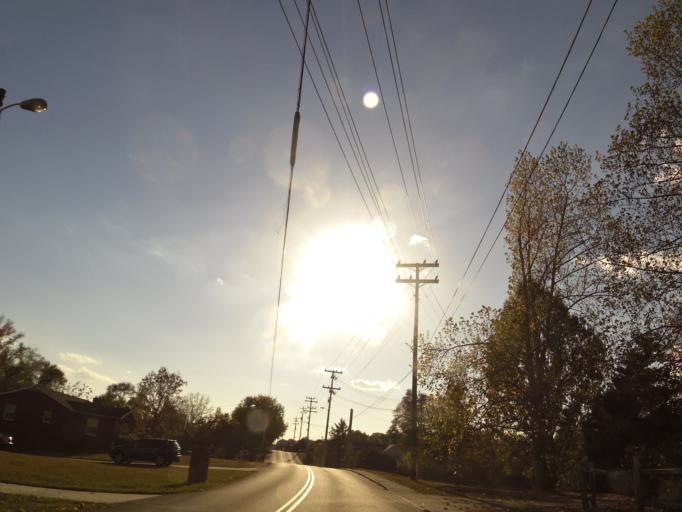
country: US
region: Tennessee
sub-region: Anderson County
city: Clinton
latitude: 36.1148
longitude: -84.1221
